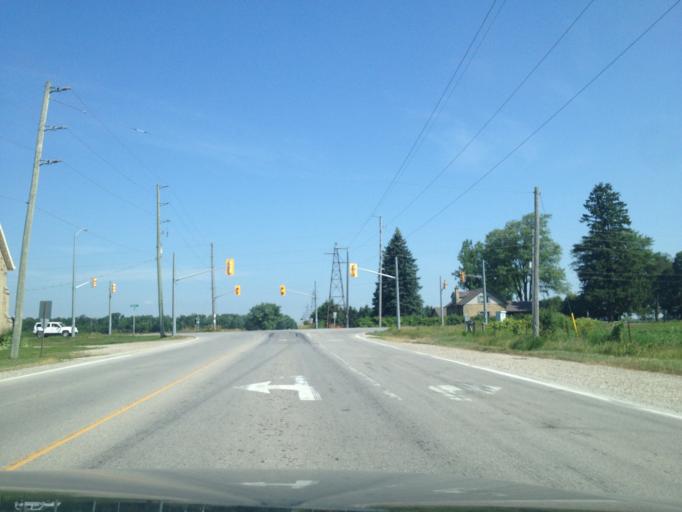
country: CA
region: Ontario
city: London
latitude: 43.0740
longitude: -81.2109
